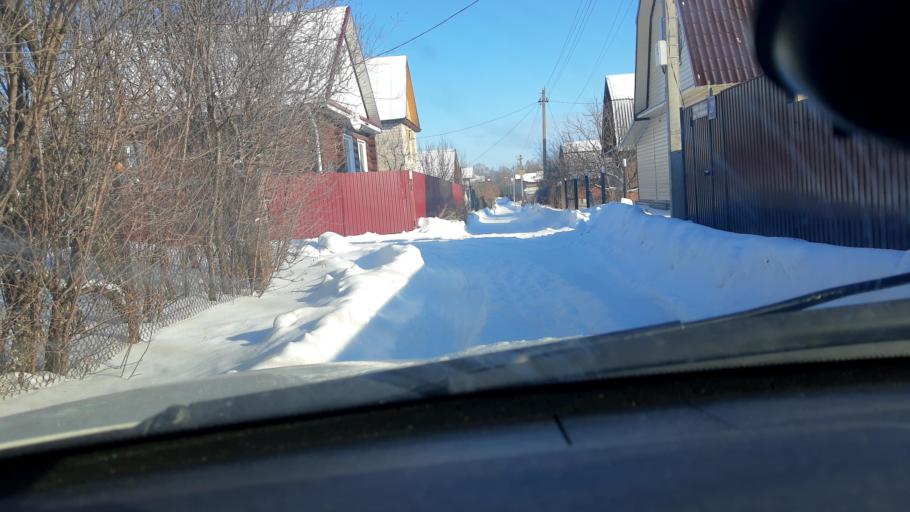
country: RU
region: Bashkortostan
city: Ufa
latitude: 54.5768
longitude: 55.8912
